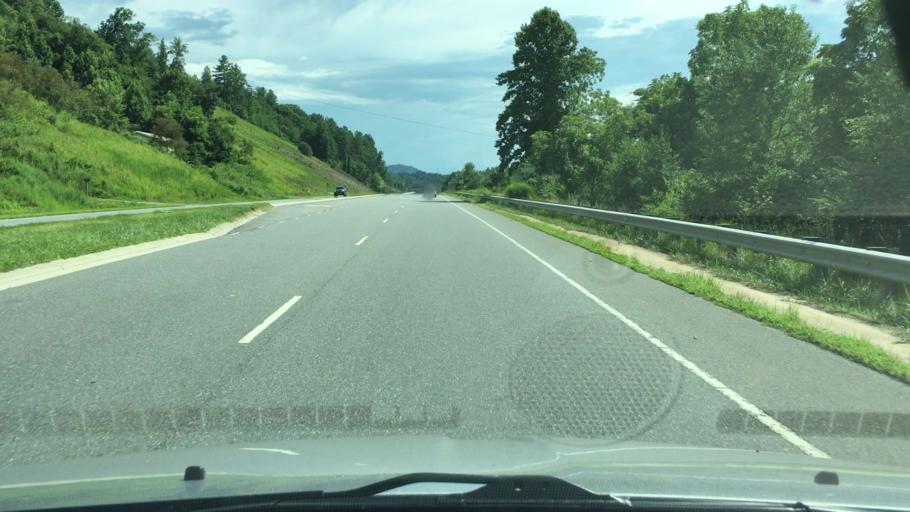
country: US
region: North Carolina
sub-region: Madison County
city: Mars Hill
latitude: 35.8732
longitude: -82.4810
